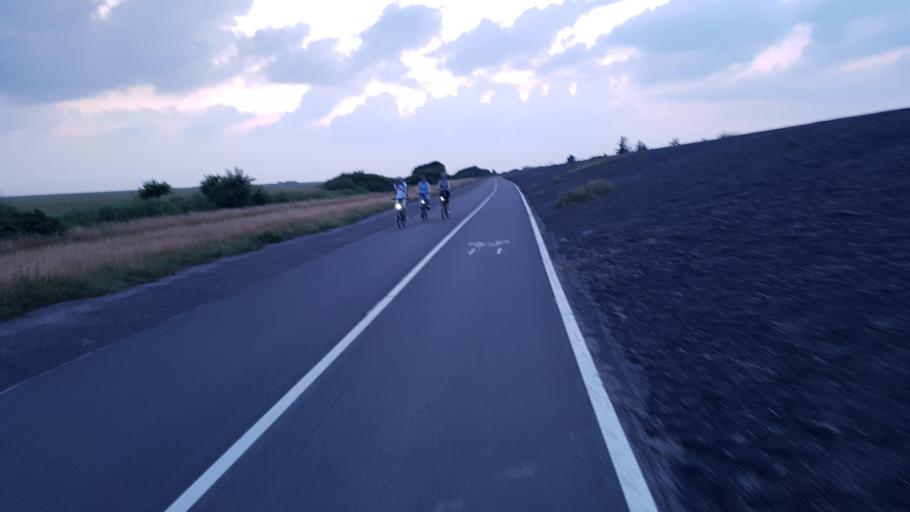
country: DE
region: Schleswig-Holstein
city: Sankt Peter-Ording
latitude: 54.2904
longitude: 8.6470
